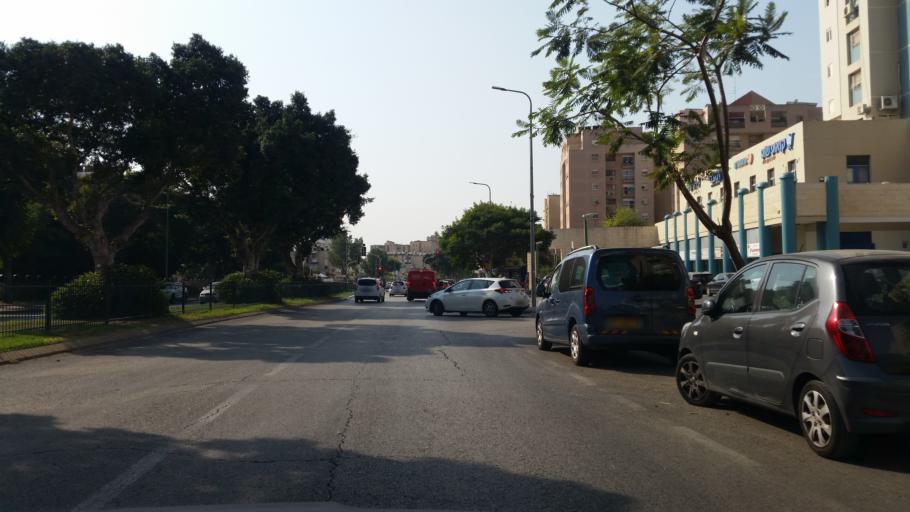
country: IL
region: Central District
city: Even Yehuda
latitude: 32.2837
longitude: 34.8542
